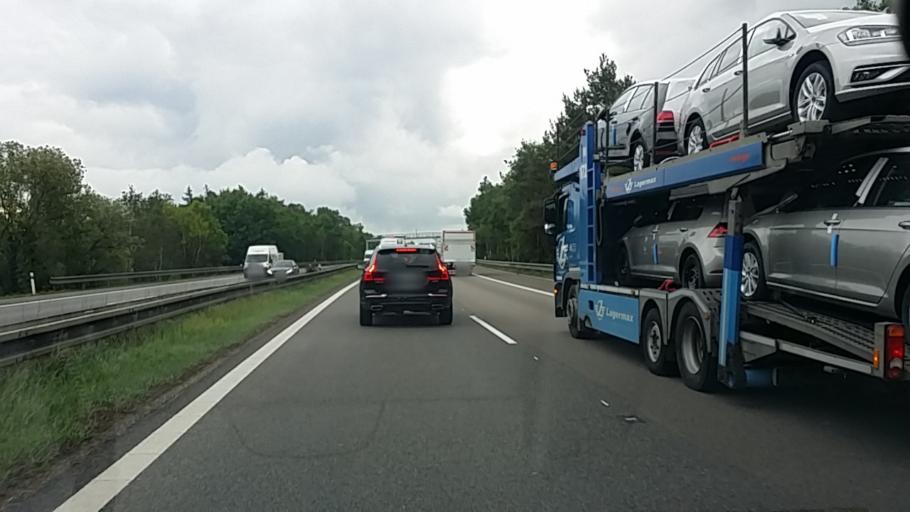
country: CZ
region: Central Bohemia
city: Zruc nad Sazavou
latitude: 49.6791
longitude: 15.1151
